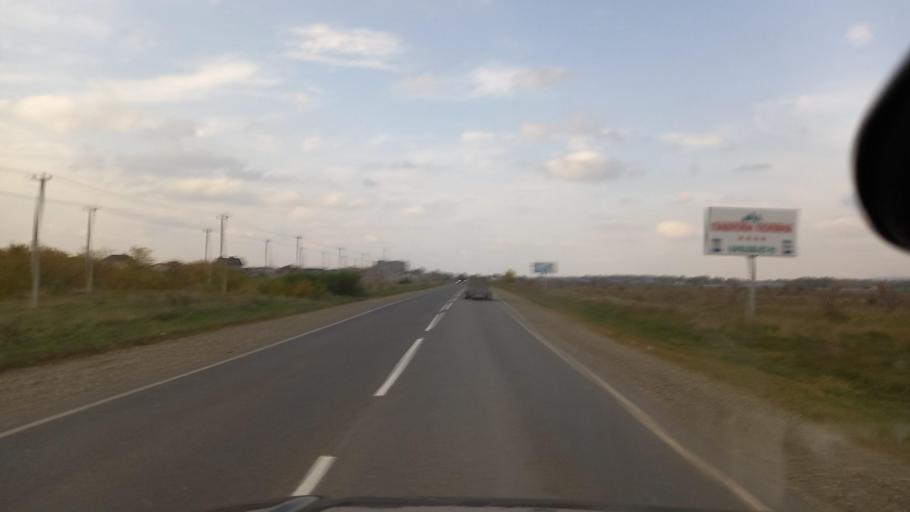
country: RU
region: Krasnodarskiy
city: Mostovskoy
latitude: 44.3837
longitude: 40.8197
